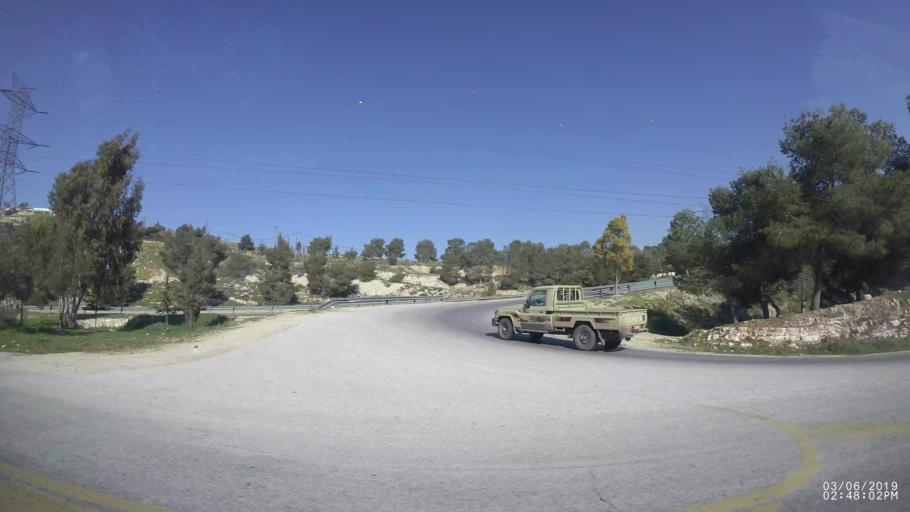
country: JO
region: Amman
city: Amman
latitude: 32.0211
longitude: 35.9585
